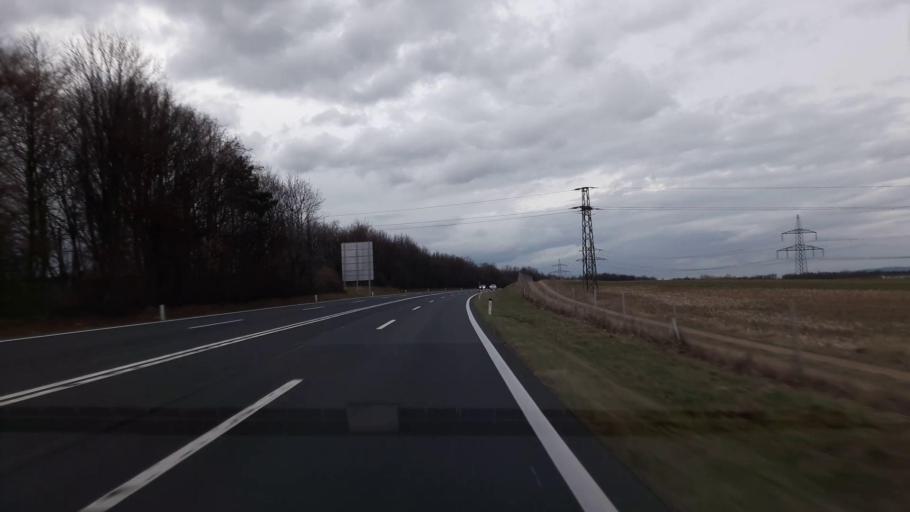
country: AT
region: Burgenland
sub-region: Politischer Bezirk Mattersburg
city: Mattersburg
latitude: 47.7324
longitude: 16.3719
